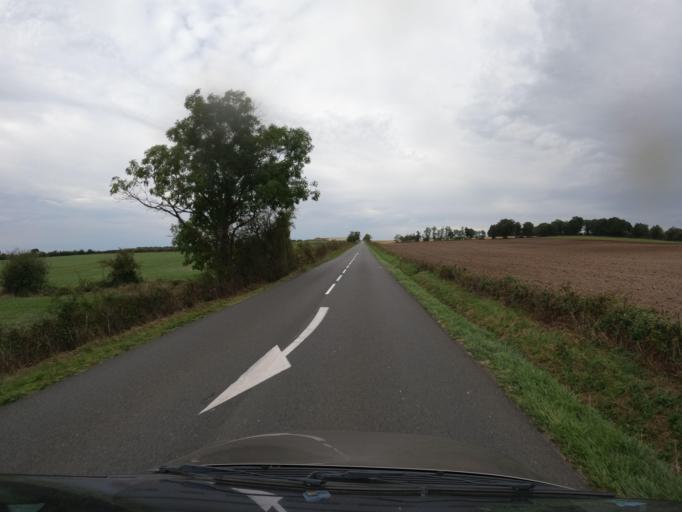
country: FR
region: Poitou-Charentes
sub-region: Departement de la Vienne
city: Saulge
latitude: 46.3779
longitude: 0.8455
